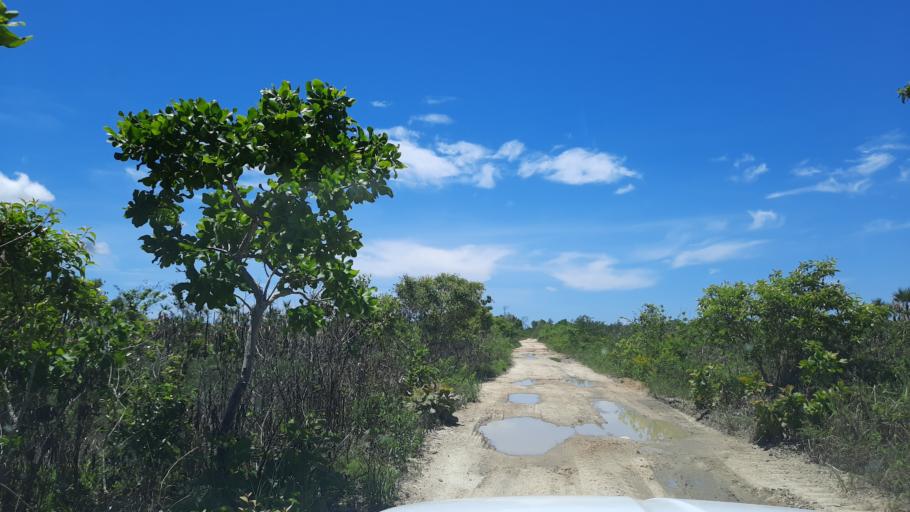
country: BZ
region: Cayo
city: Belmopan
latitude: 17.3799
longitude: -88.4907
